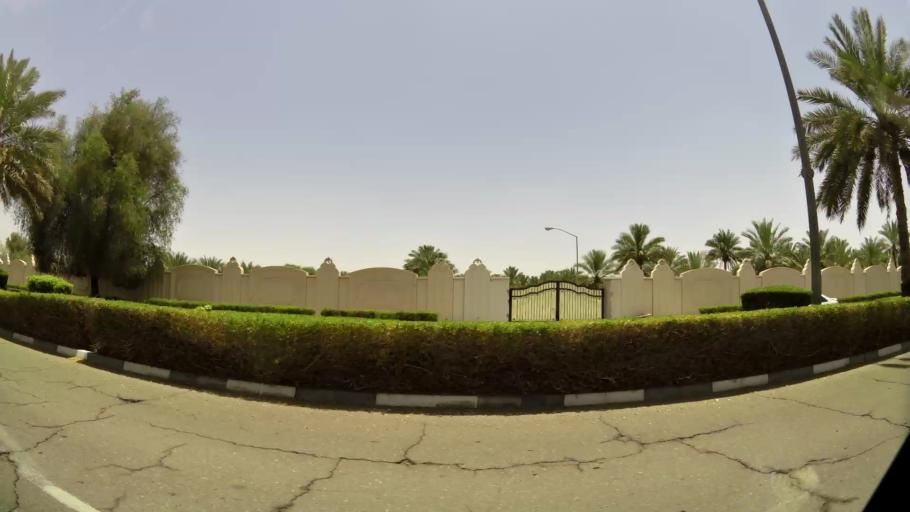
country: OM
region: Al Buraimi
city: Al Buraymi
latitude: 24.2719
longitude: 55.7665
